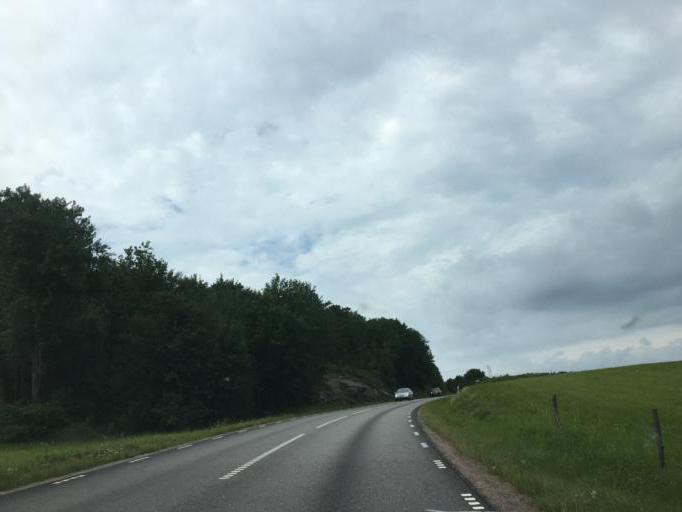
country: SE
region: Vaestra Goetaland
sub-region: Sotenas Kommun
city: Hunnebostrand
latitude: 58.4136
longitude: 11.2824
